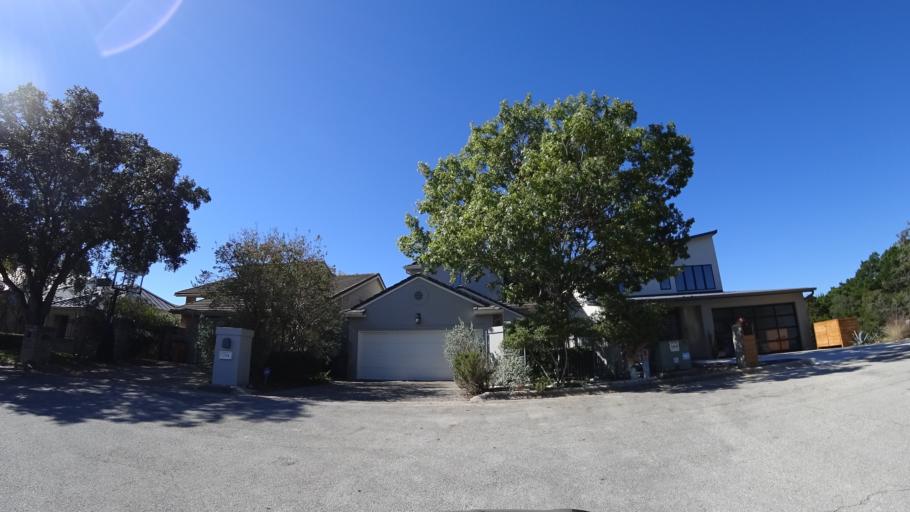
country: US
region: Texas
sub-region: Travis County
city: West Lake Hills
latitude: 30.3511
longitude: -97.7799
